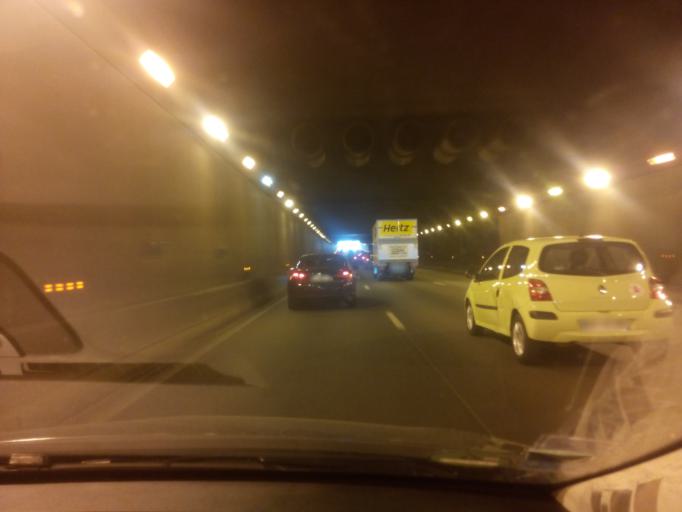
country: FR
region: Ile-de-France
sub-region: Departement des Hauts-de-Seine
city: Malakoff
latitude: 48.8251
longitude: 2.3036
